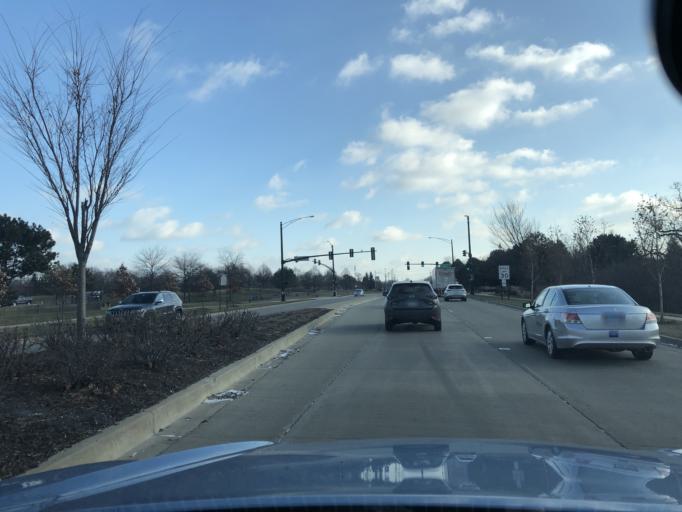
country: US
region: Illinois
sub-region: Cook County
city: Northfield
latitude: 42.1054
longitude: -87.7963
